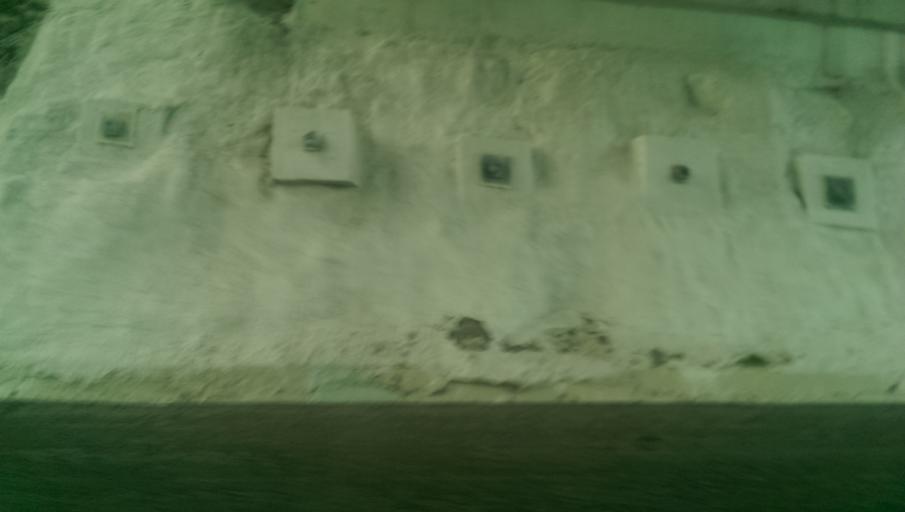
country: MX
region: Queretaro
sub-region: Queretaro
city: Santiago de Queretaro
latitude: 20.5846
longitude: -100.3560
